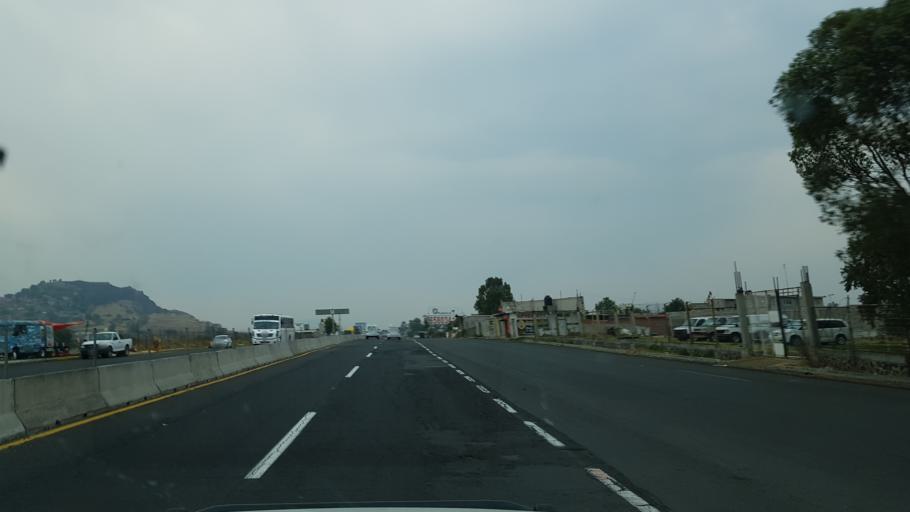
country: MX
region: Mexico
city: Cocotitlan
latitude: 19.2331
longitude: -98.8462
